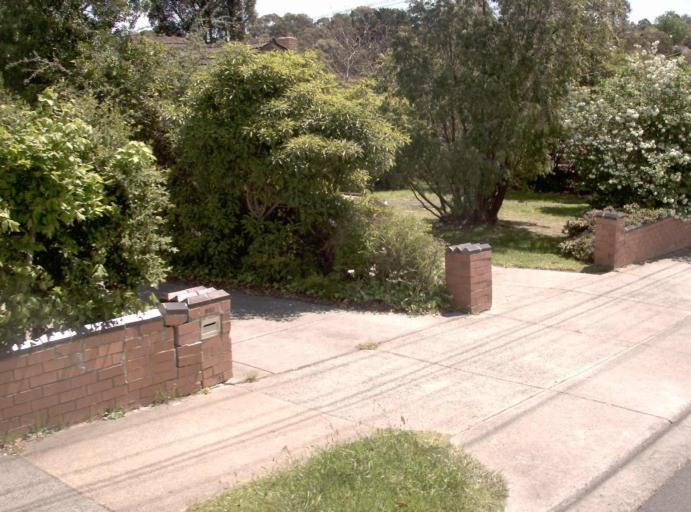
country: AU
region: Victoria
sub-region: Monash
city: Notting Hill
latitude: -37.8855
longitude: 145.1458
